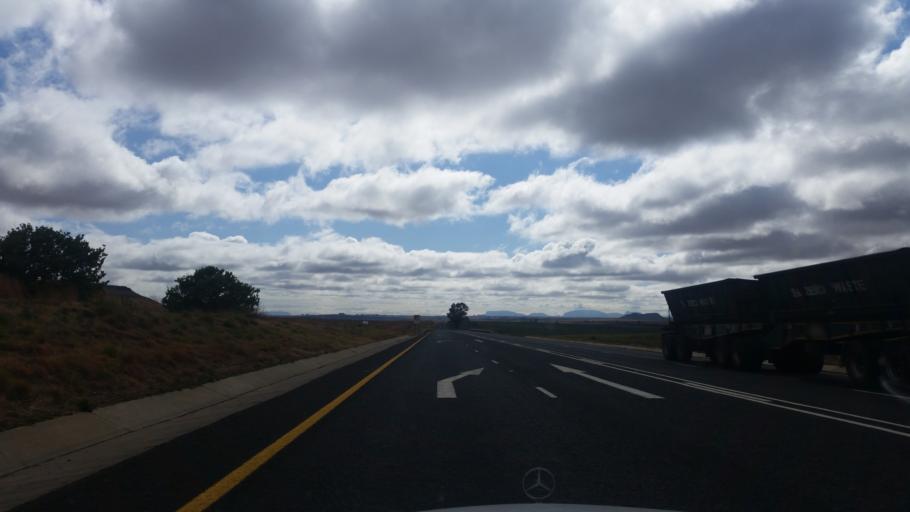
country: ZA
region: Orange Free State
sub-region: Thabo Mofutsanyana District Municipality
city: Phuthaditjhaba
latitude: -28.3061
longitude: 28.7807
